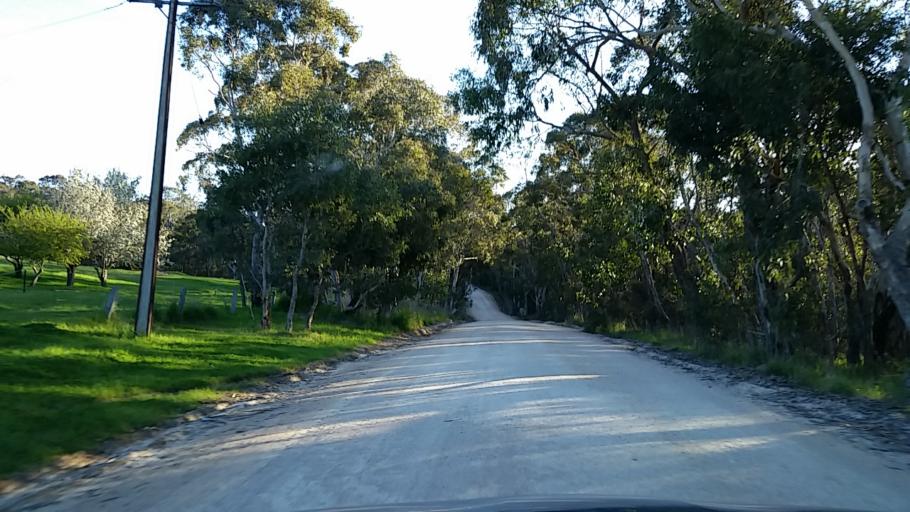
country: AU
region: South Australia
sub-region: Alexandrina
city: Mount Compass
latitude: -35.2969
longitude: 138.6842
